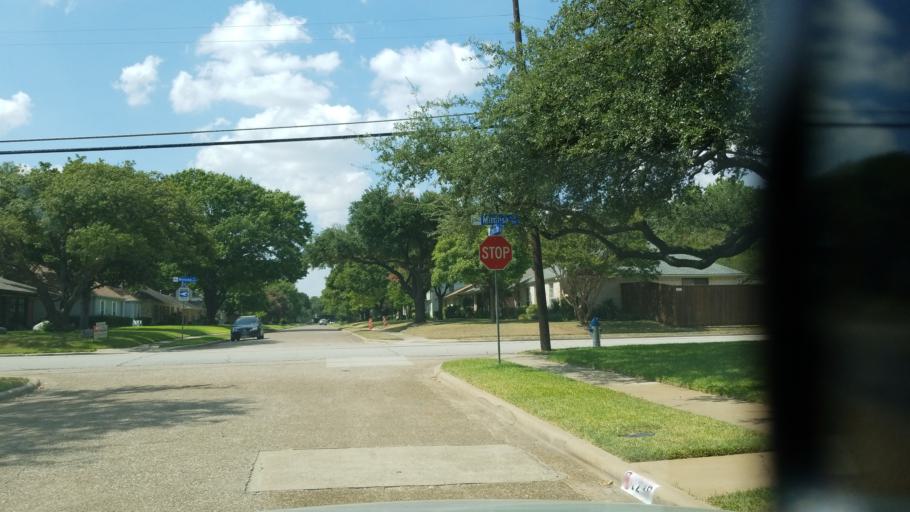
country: US
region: Texas
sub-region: Dallas County
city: Richardson
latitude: 32.9655
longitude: -96.7621
